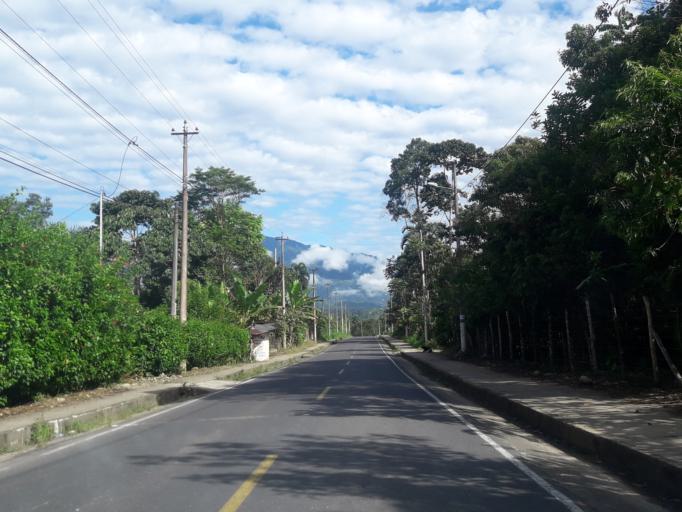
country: EC
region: Napo
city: Tena
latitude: -0.9833
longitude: -77.8421
